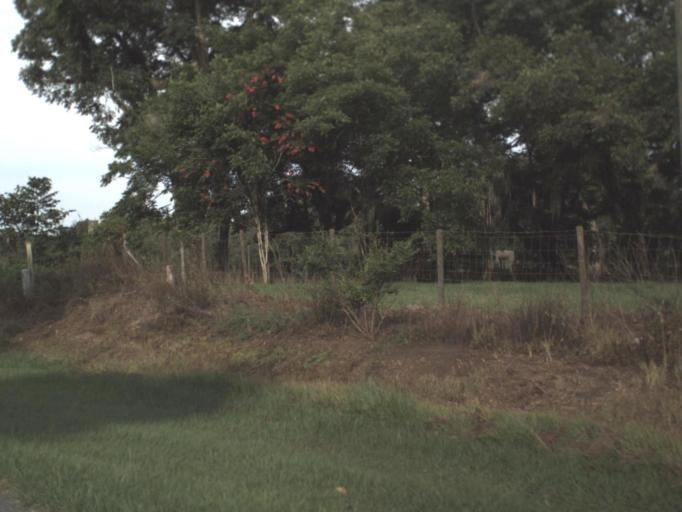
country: US
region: Florida
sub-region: Madison County
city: Madison
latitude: 30.4114
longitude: -83.6411
